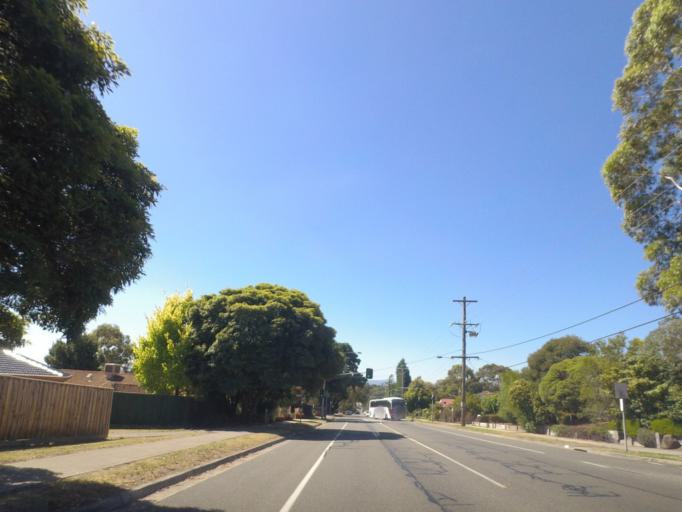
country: AU
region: Victoria
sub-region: Maroondah
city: Warranwood
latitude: -37.7880
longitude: 145.2479
